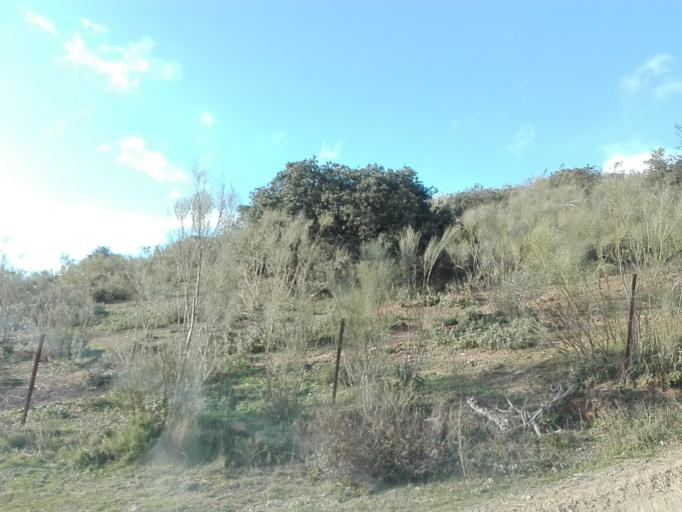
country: ES
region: Extremadura
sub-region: Provincia de Badajoz
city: Trasierra
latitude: 38.2040
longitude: -5.9999
